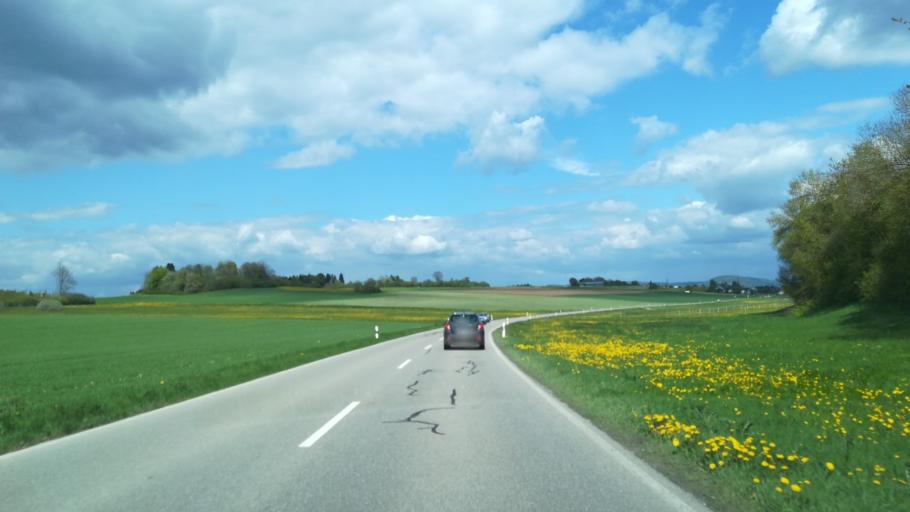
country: DE
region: Baden-Wuerttemberg
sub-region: Freiburg Region
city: Bonndorf im Schwarzwald
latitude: 47.8225
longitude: 8.3767
